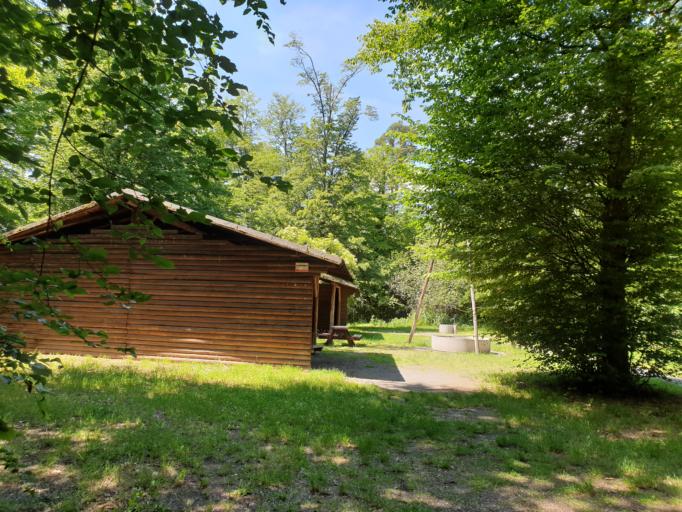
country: DE
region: Baden-Wuerttemberg
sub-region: Karlsruhe Region
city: Ubstadt-Weiher
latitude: 49.1918
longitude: 8.6085
